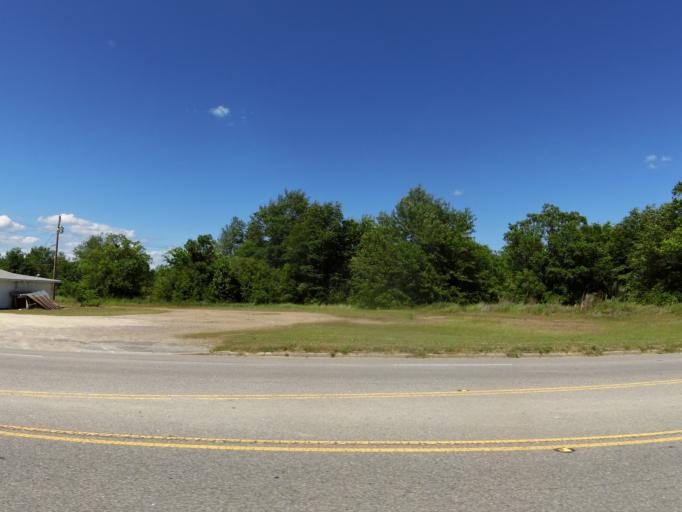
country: US
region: South Carolina
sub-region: Aiken County
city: Aiken
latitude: 33.5468
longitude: -81.6839
